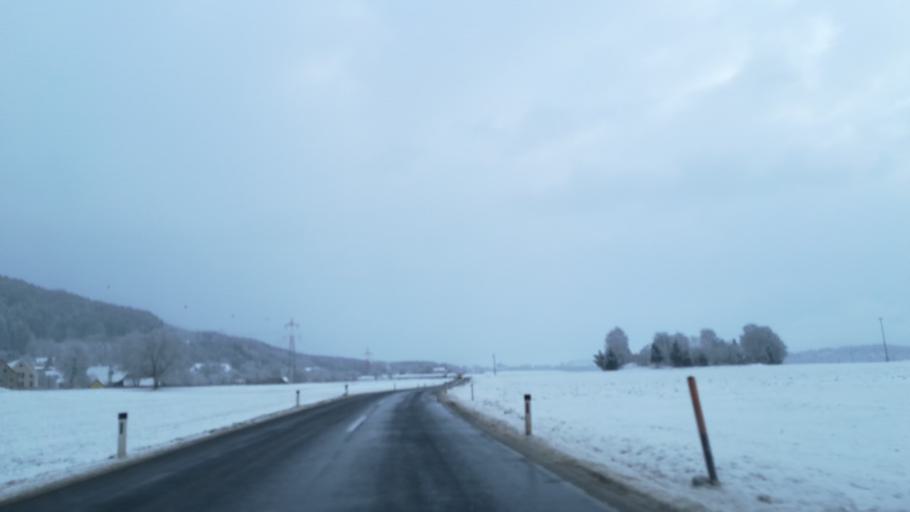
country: AT
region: Styria
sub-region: Politischer Bezirk Murtal
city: Fohnsdorf
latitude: 47.2059
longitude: 14.6372
